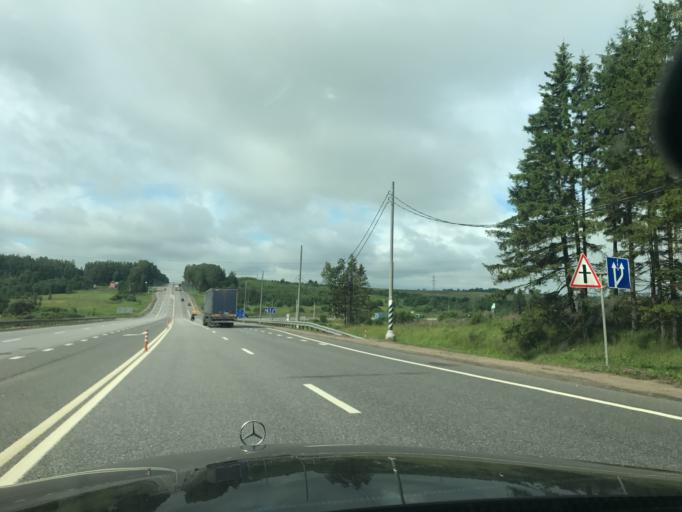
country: RU
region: Smolensk
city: Kardymovo
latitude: 55.0158
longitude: 32.2984
